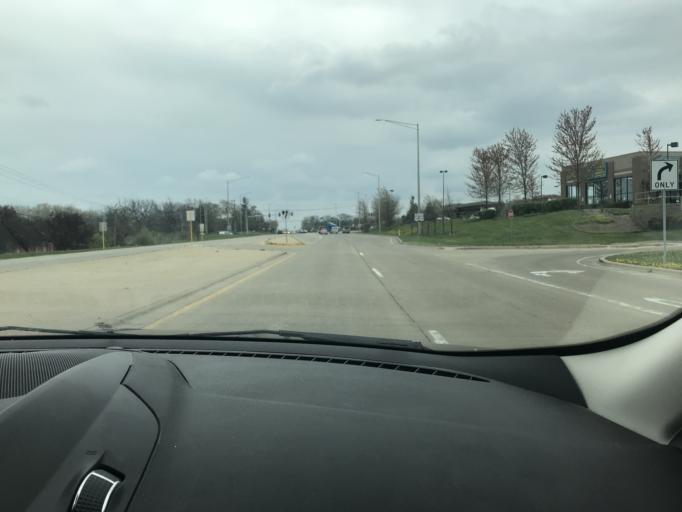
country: US
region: Illinois
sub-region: Kendall County
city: Boulder Hill
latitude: 41.7203
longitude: -88.2833
